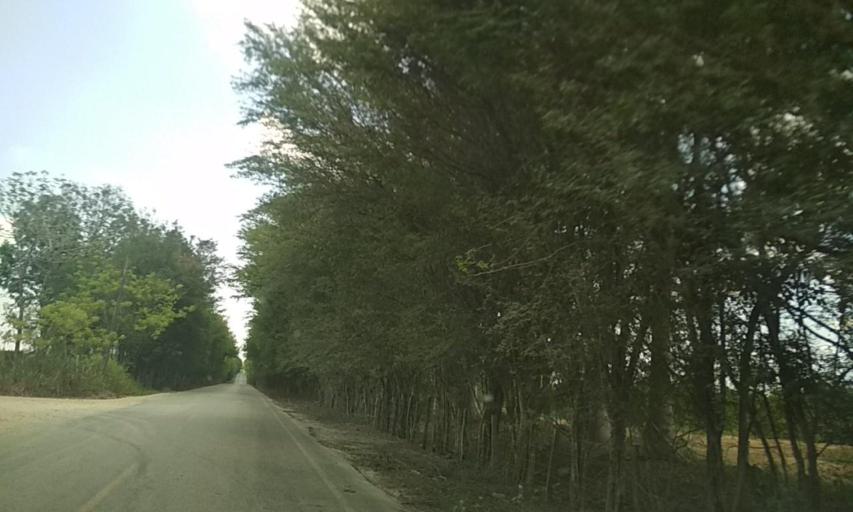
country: MX
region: Tabasco
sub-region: Huimanguillo
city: Paso de la Mina 2da. Seccion (Barrial)
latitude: 17.7704
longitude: -93.6463
